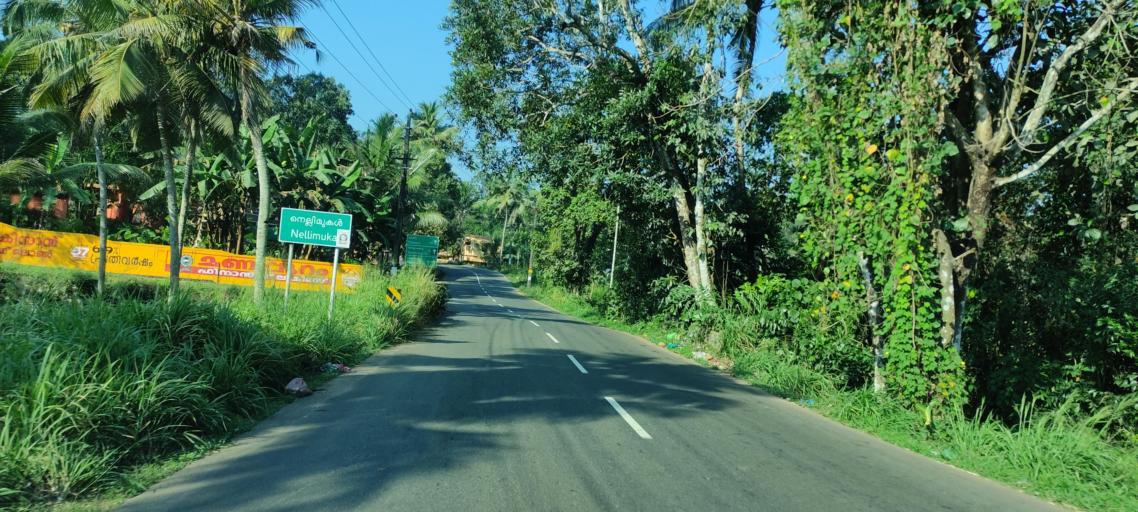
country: IN
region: Kerala
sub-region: Pattanamtitta
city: Adur
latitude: 9.1230
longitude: 76.7017
